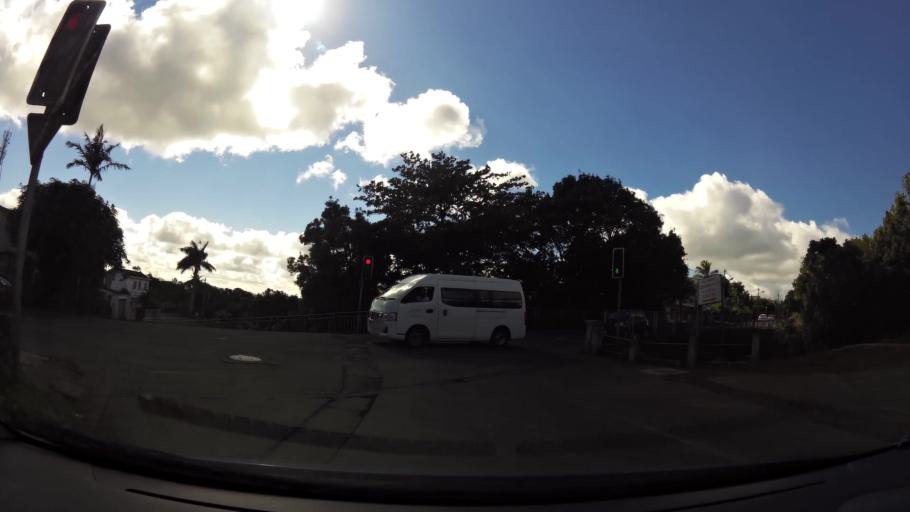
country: MU
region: Plaines Wilhems
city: Curepipe
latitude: -20.3082
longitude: 57.5138
